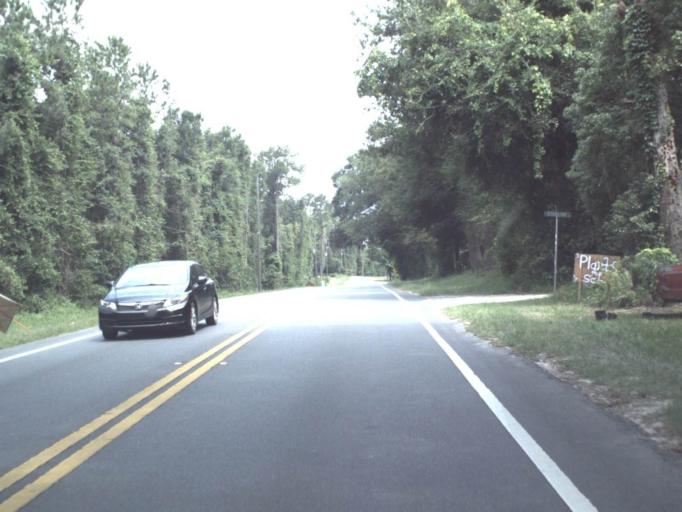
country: US
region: Florida
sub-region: Clay County
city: Keystone Heights
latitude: 29.6873
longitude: -82.0376
